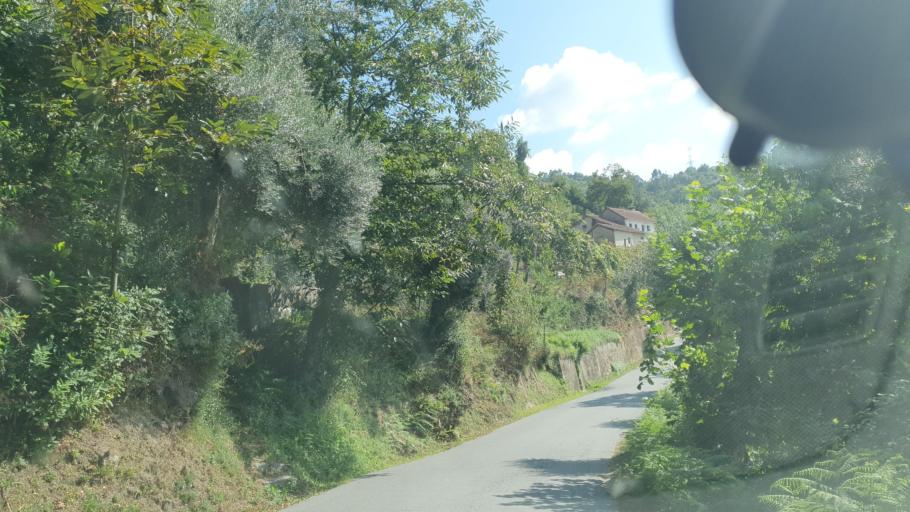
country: PT
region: Braga
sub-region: Vieira do Minho
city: Real
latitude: 41.6703
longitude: -8.1661
